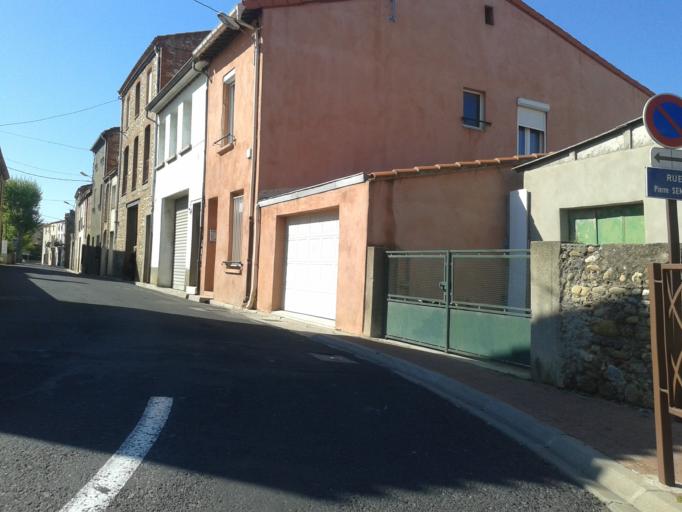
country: FR
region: Languedoc-Roussillon
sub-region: Departement des Pyrenees-Orientales
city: Le Soler
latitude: 42.6815
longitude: 2.7954
